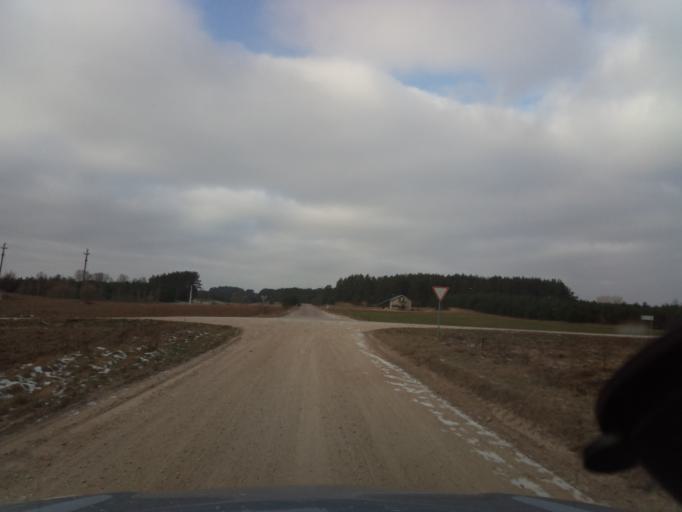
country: LT
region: Alytaus apskritis
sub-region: Alytaus rajonas
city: Daugai
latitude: 54.3244
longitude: 24.3163
